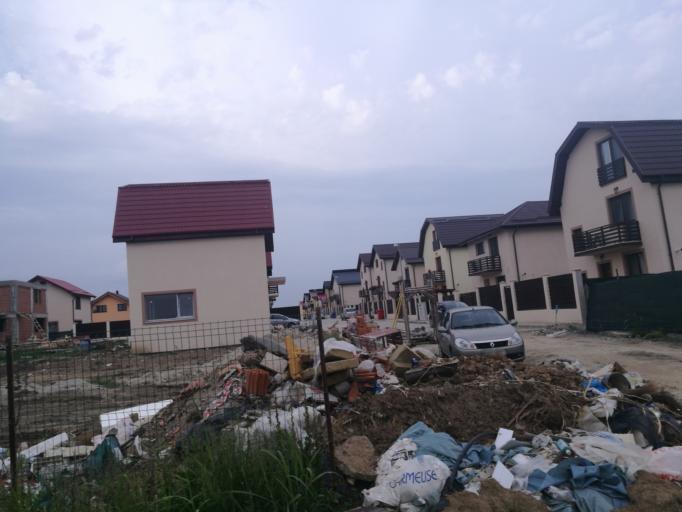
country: RO
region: Ilfov
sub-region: Comuna Vidra
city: Vidra
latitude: 44.2755
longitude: 26.1832
